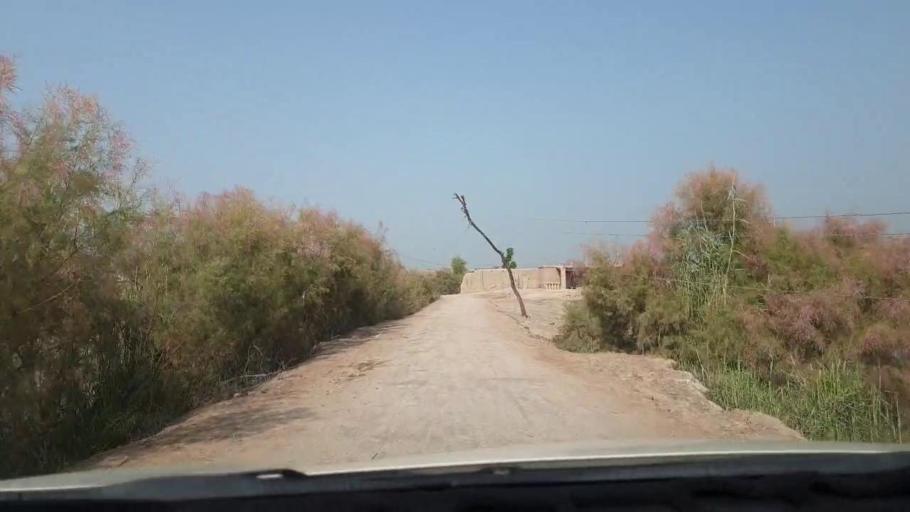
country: PK
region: Sindh
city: Goth Garelo
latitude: 27.4585
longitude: 68.1210
